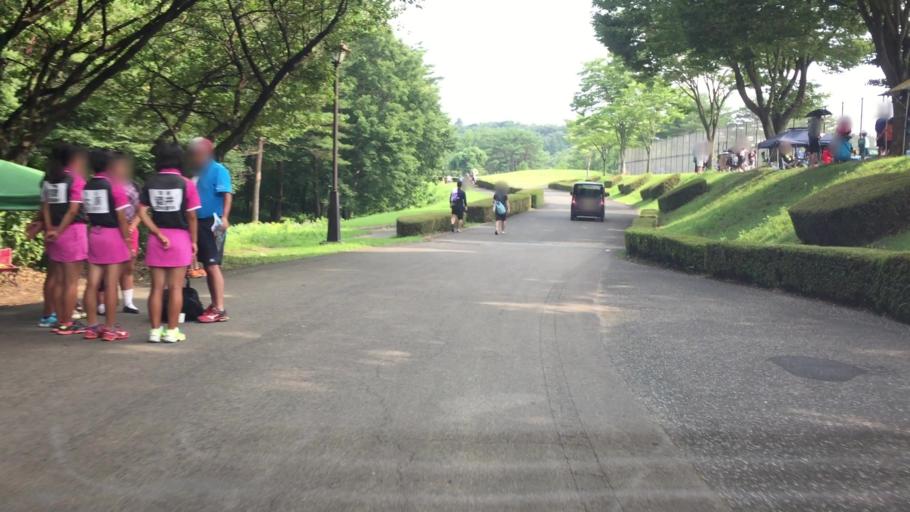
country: JP
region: Tochigi
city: Otawara
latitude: 36.9290
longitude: 139.9522
